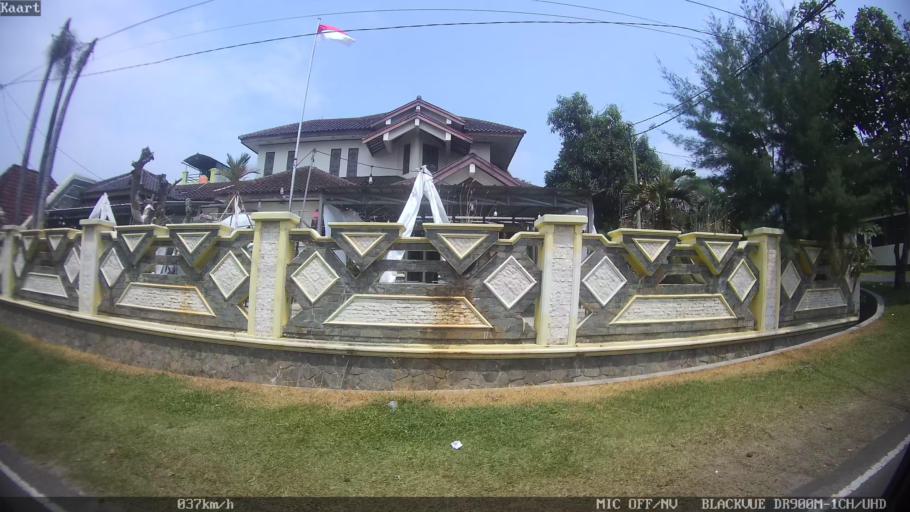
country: ID
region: Lampung
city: Bandarlampung
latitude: -5.4264
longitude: 105.2718
